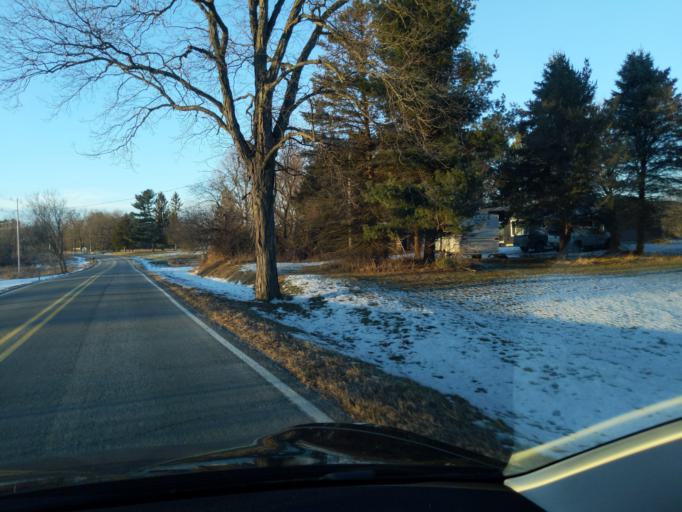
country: US
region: Michigan
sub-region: Ingham County
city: Stockbridge
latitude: 42.5057
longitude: -84.2564
